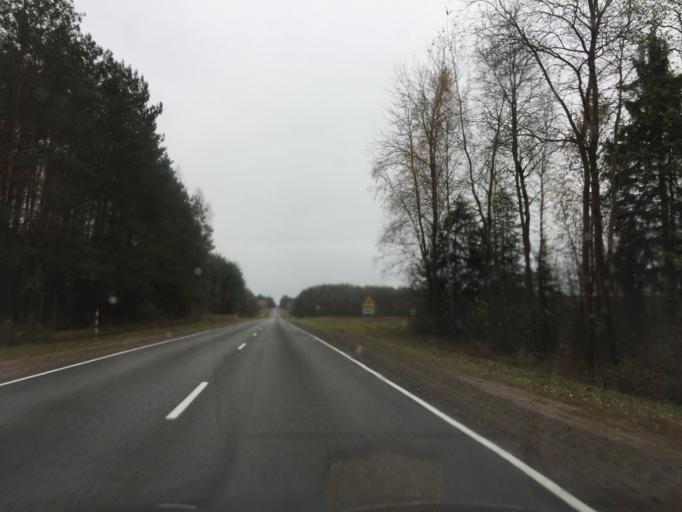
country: BY
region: Mogilev
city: Chavusy
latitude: 53.7337
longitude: 31.1142
